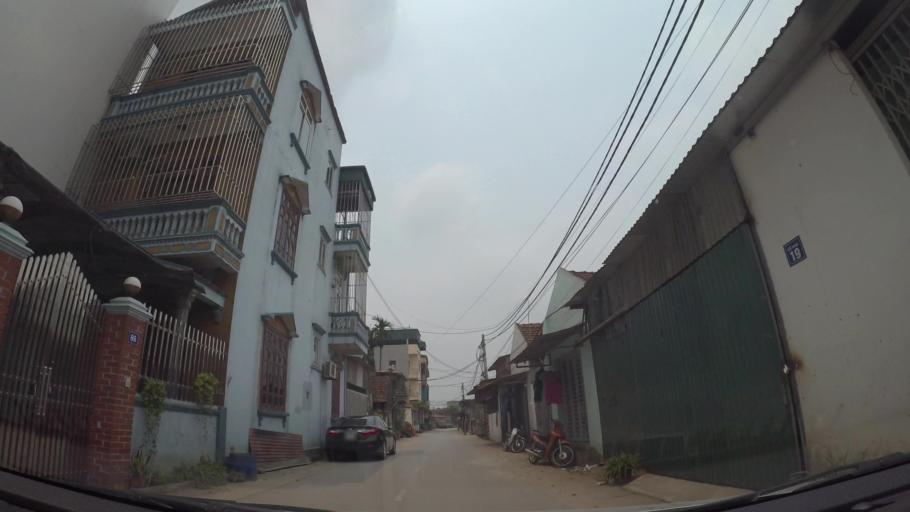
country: VN
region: Ha Noi
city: Ha Dong
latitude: 20.9914
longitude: 105.7413
